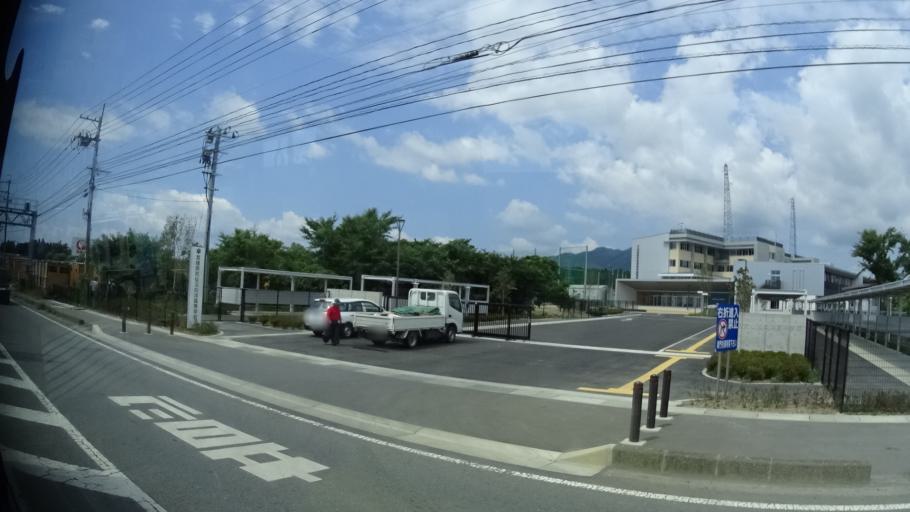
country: JP
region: Iwate
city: Ofunato
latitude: 38.8340
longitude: 141.5783
